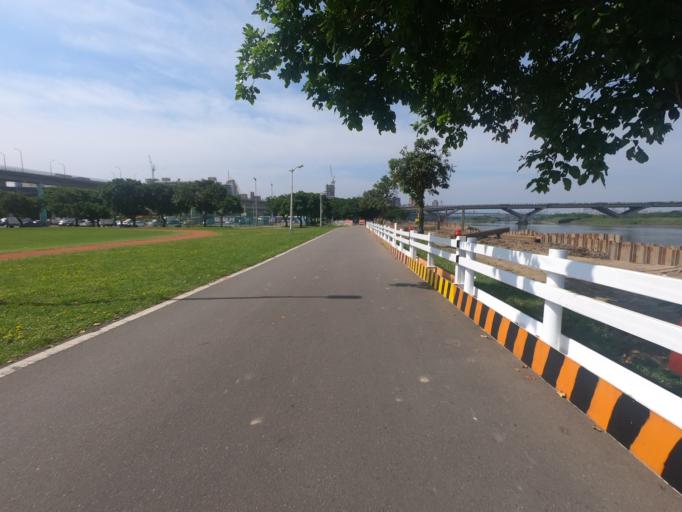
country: TW
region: Taipei
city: Taipei
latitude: 25.0532
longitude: 121.5060
